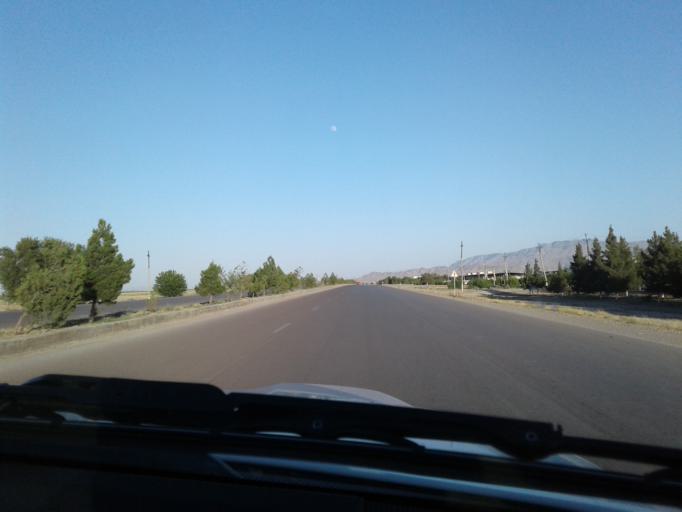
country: TM
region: Ahal
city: Baharly
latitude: 38.3242
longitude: 57.5903
